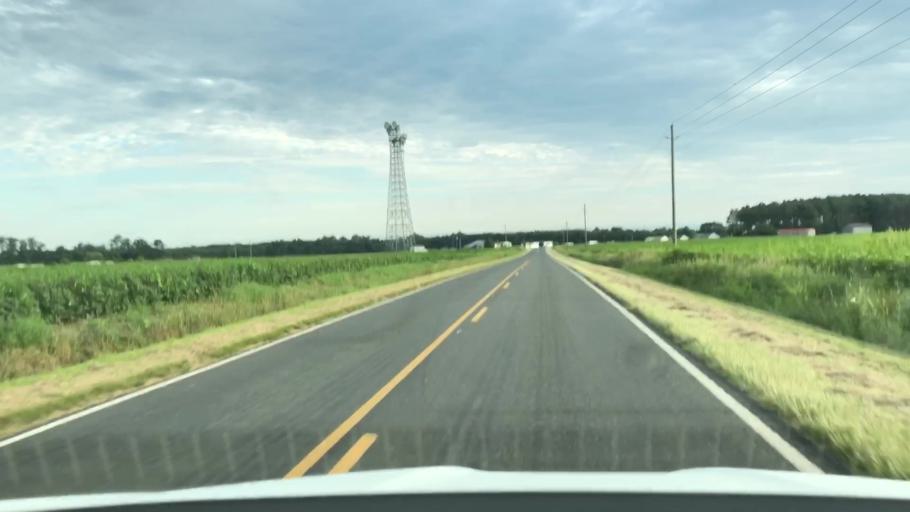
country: US
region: North Carolina
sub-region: Jones County
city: Maysville
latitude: 34.9921
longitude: -77.2806
